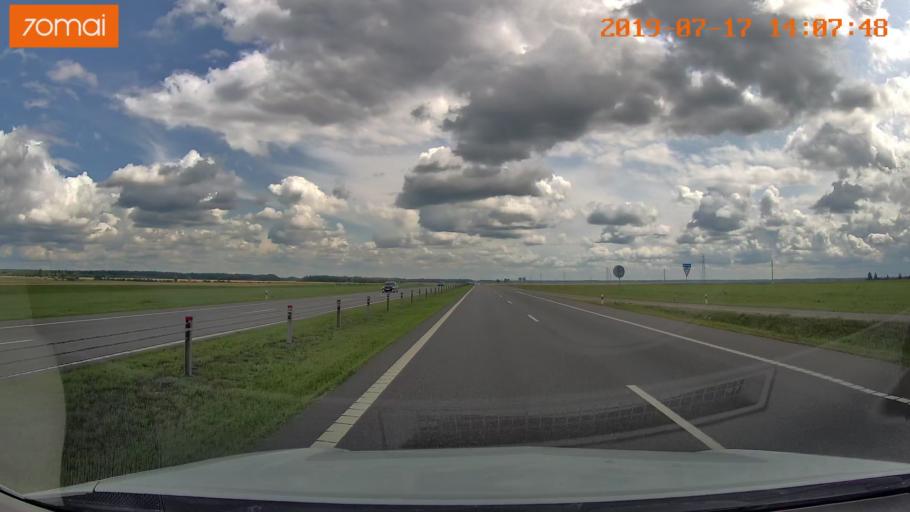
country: BY
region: Mogilev
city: Yalizava
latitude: 53.2422
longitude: 28.9507
